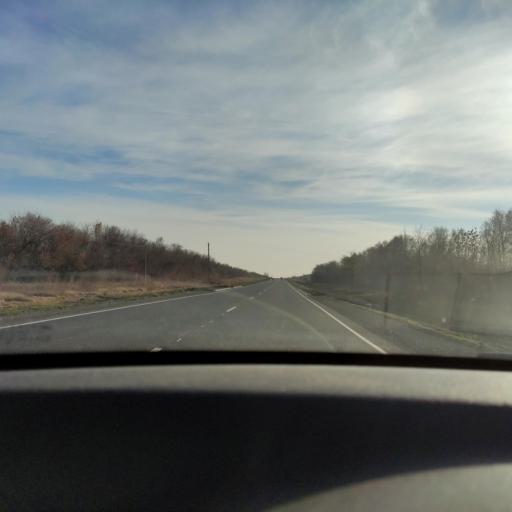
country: RU
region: Samara
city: Krasnoarmeyskoye
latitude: 52.8152
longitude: 50.0106
